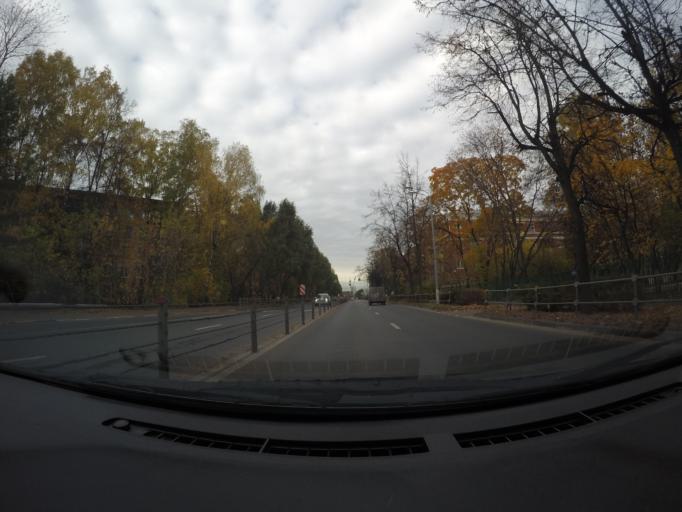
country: RU
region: Moskovskaya
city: Mytishchi
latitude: 55.9148
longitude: 37.7290
